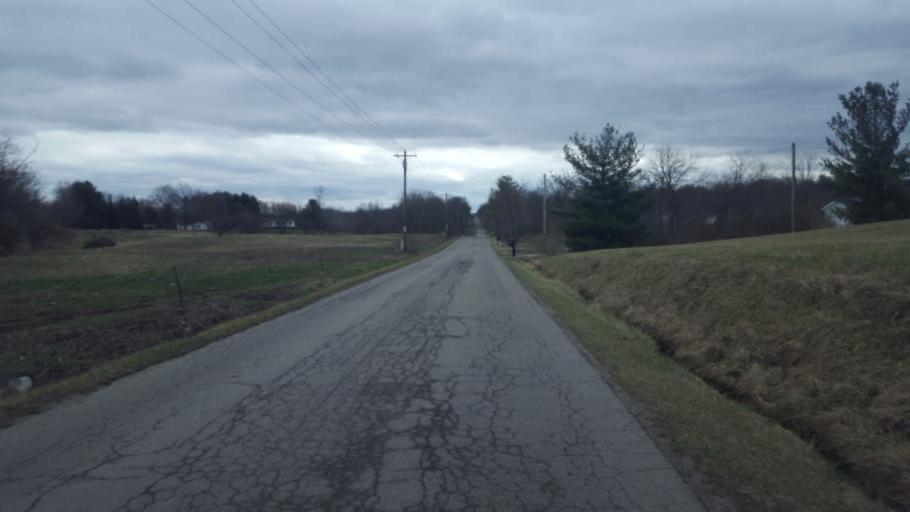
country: US
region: Ohio
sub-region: Knox County
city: Centerburg
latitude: 40.4334
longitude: -82.6829
